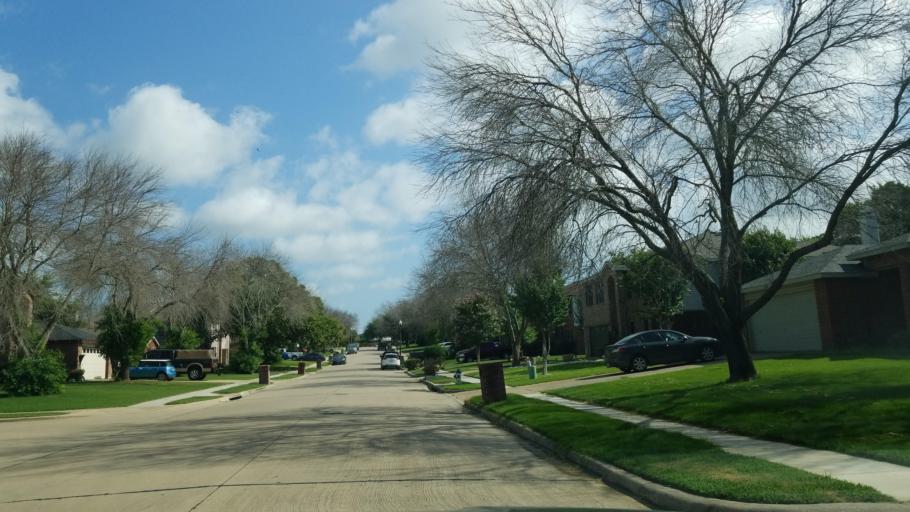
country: US
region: Texas
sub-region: Denton County
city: Copper Canyon
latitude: 33.1360
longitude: -97.1140
